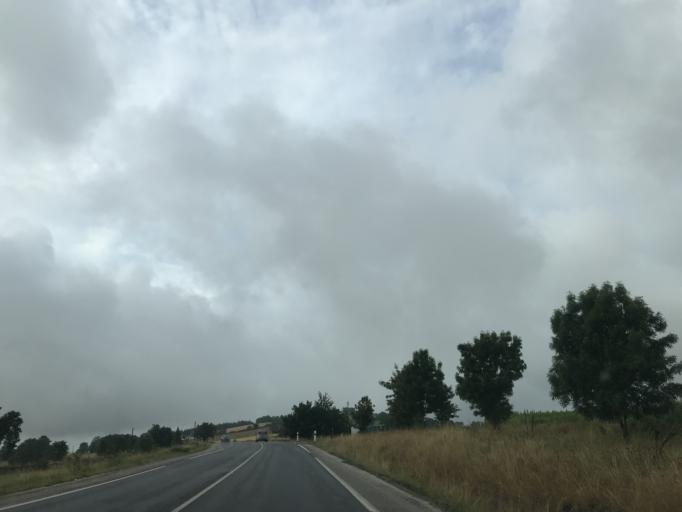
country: FR
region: Auvergne
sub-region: Departement de la Haute-Loire
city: Saint-Paulien
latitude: 45.1279
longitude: 3.8196
